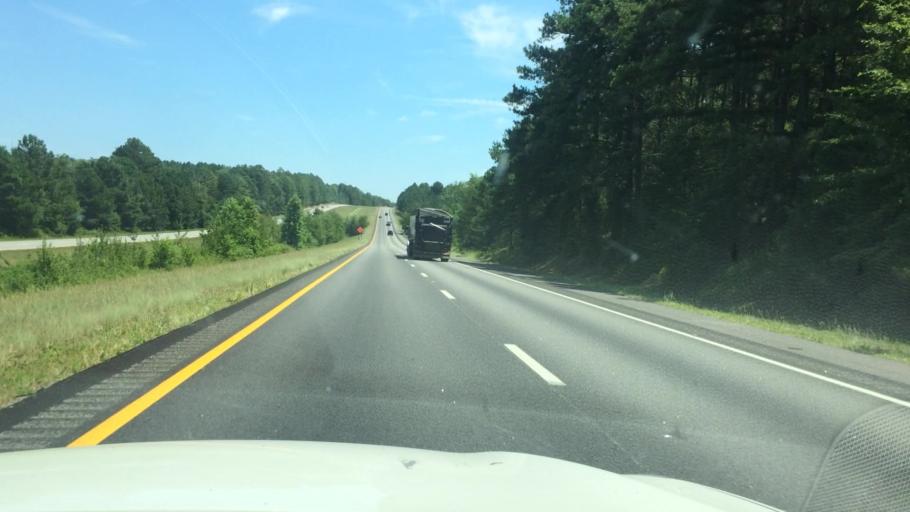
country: US
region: South Carolina
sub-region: Lexington County
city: Red Bank
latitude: 33.9119
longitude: -81.3249
